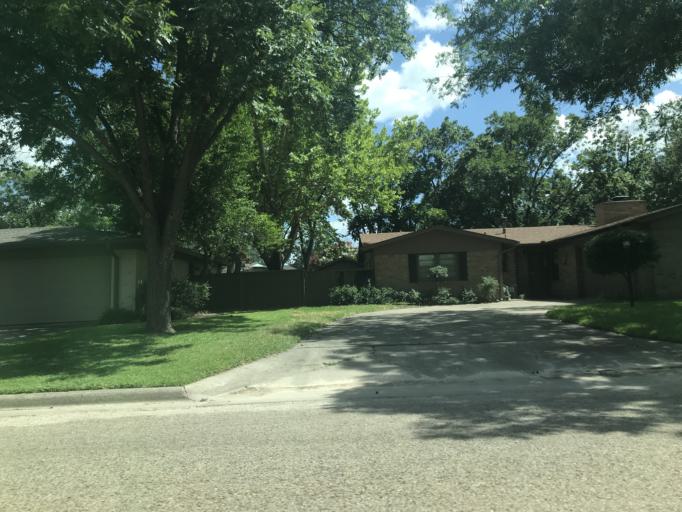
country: US
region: Texas
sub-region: Taylor County
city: Abilene
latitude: 32.4227
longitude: -99.7609
